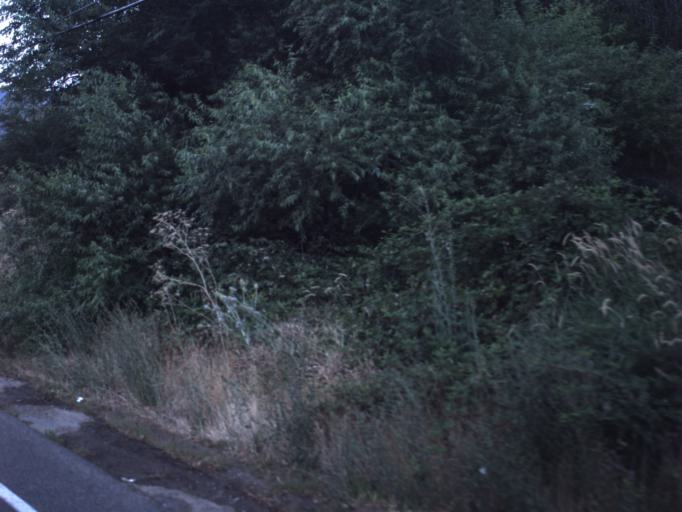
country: US
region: Utah
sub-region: Davis County
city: Farmington
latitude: 40.9549
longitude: -111.8833
